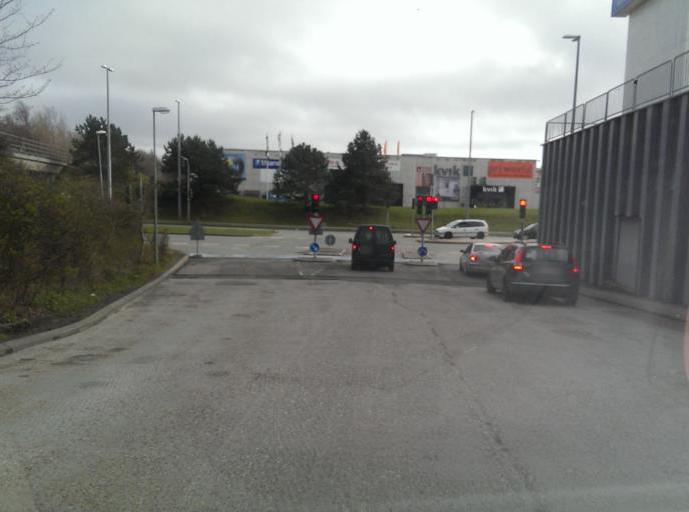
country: DK
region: South Denmark
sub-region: Esbjerg Kommune
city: Esbjerg
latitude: 55.5093
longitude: 8.4570
